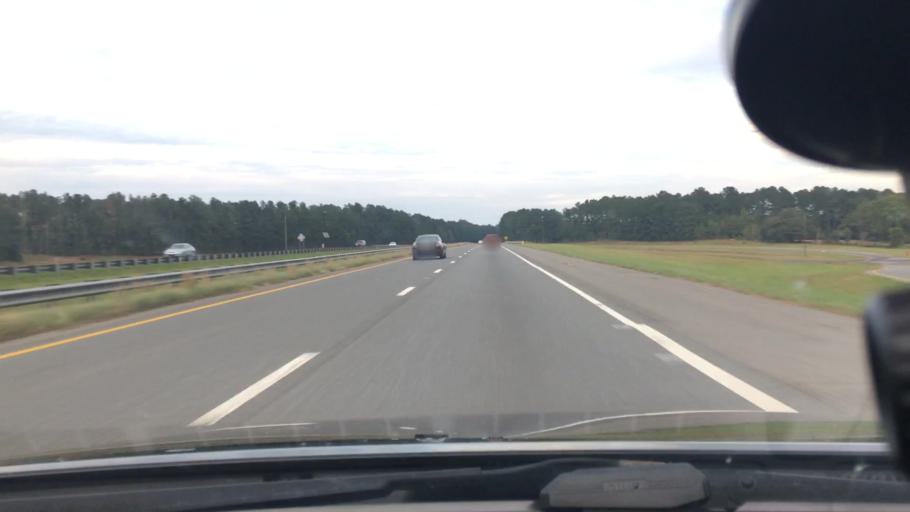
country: US
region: North Carolina
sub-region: Chatham County
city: Farmville
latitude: 35.5590
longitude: -79.1547
